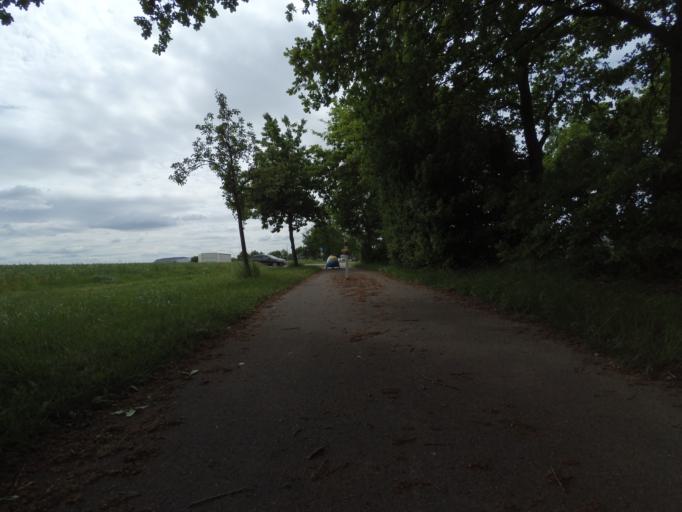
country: DE
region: Lower Saxony
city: Hagenburg
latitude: 52.4466
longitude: 9.3569
